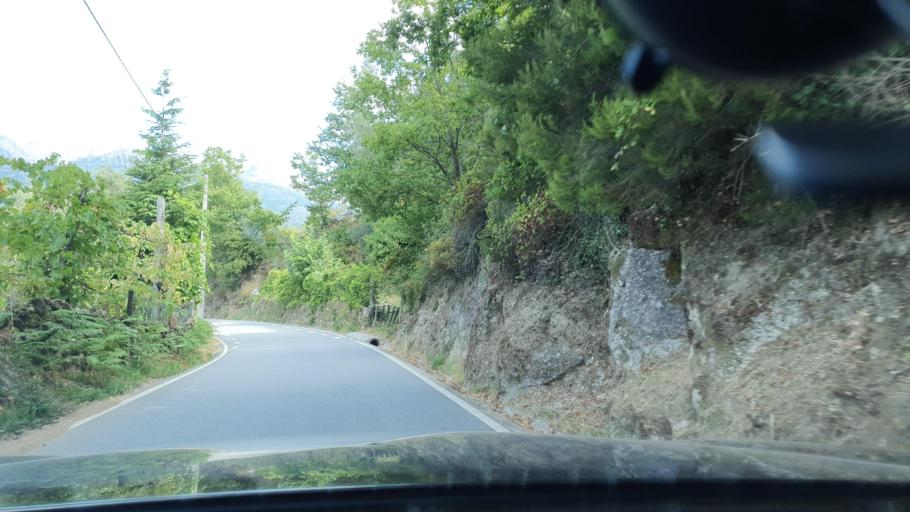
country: PT
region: Braga
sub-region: Vieira do Minho
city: Vieira do Minho
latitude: 41.6848
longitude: -8.0989
